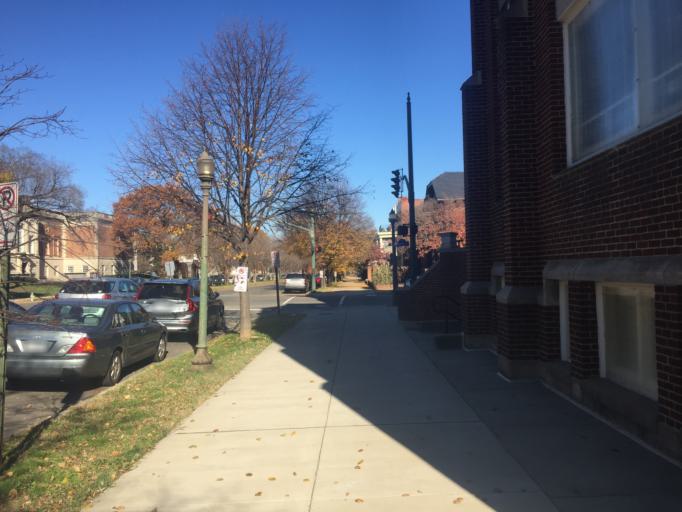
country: US
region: Virginia
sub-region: City of Richmond
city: Richmond
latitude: 37.5545
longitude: -77.4744
